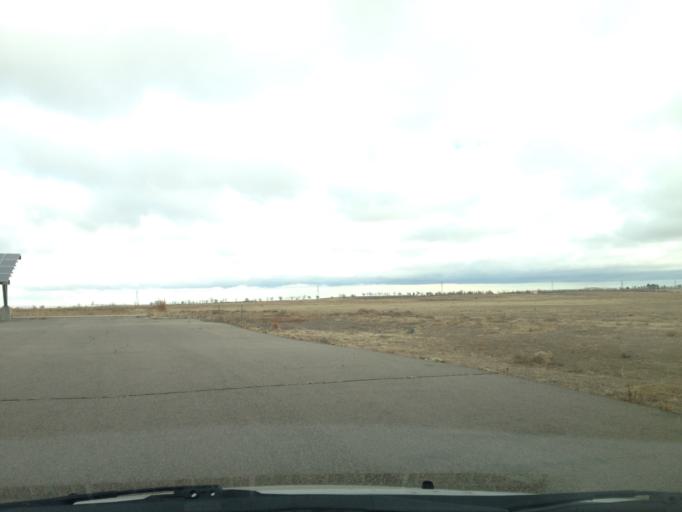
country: US
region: Colorado
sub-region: Adams County
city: Derby
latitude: 39.8141
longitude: -104.8791
